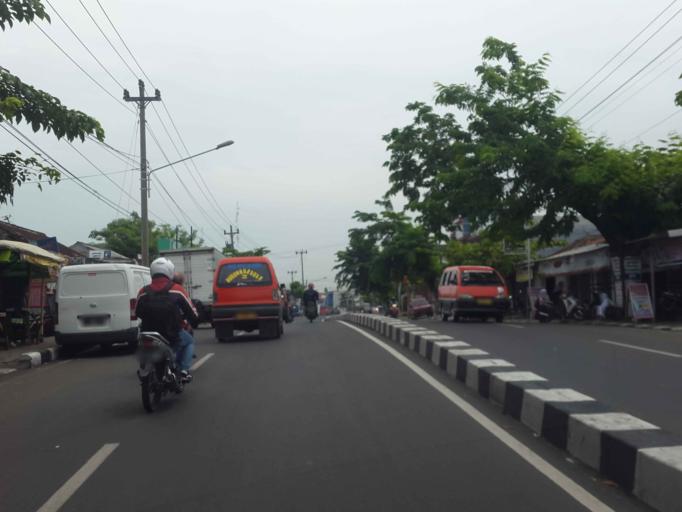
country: ID
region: Central Java
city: Semarang
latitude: -7.0130
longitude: 110.4489
